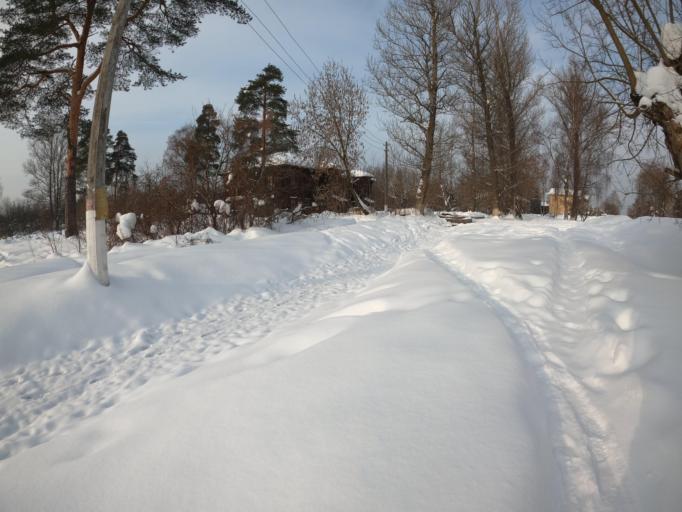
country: RU
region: Moskovskaya
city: Elektrogorsk
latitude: 55.8921
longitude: 38.7701
